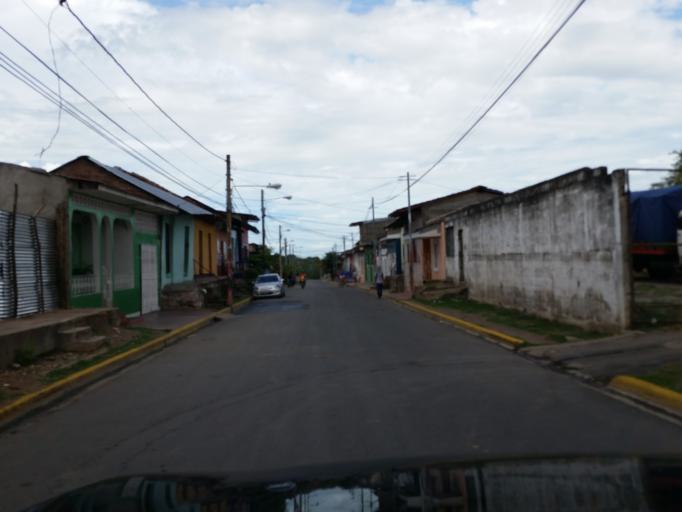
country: NI
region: Granada
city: Granada
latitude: 11.9318
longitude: -85.9496
